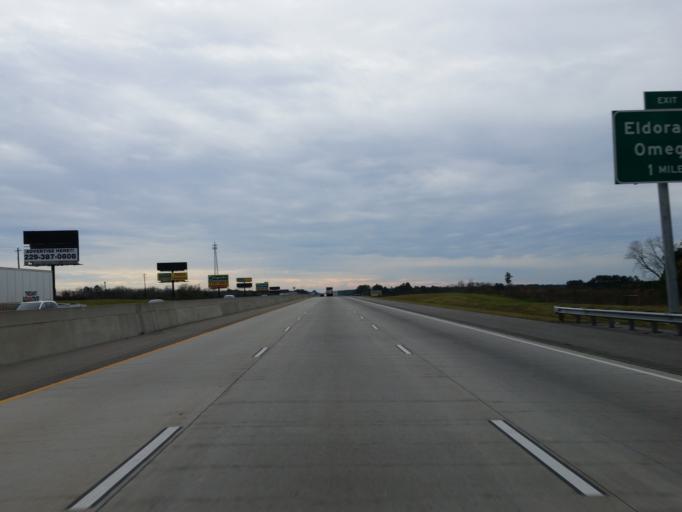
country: US
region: Georgia
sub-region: Tift County
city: Unionville
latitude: 31.3785
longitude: -83.4952
